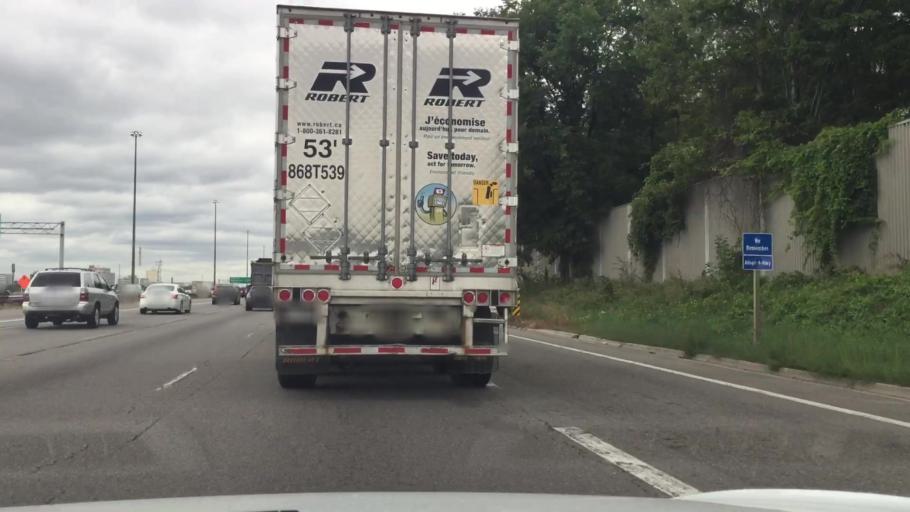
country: CA
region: Ontario
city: Scarborough
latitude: 43.7801
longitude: -79.2664
